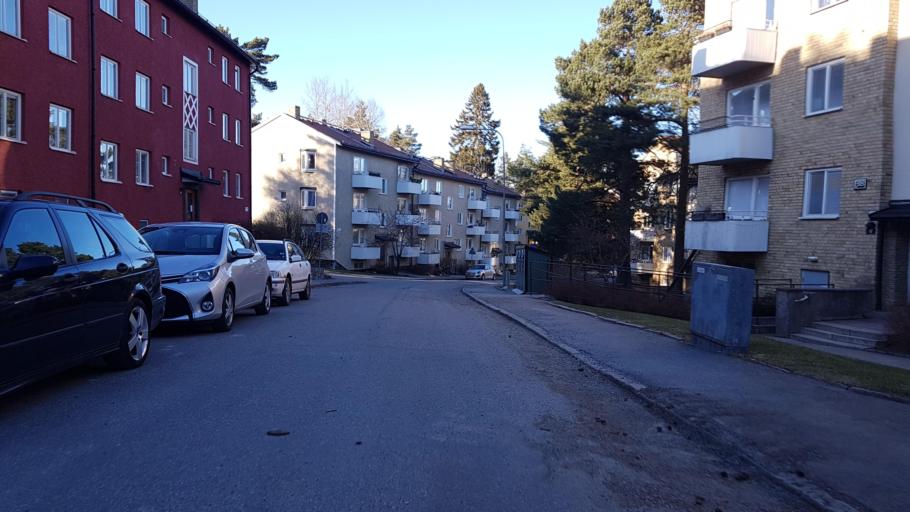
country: SE
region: Stockholm
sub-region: Stockholms Kommun
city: Arsta
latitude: 59.2651
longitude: 18.0755
